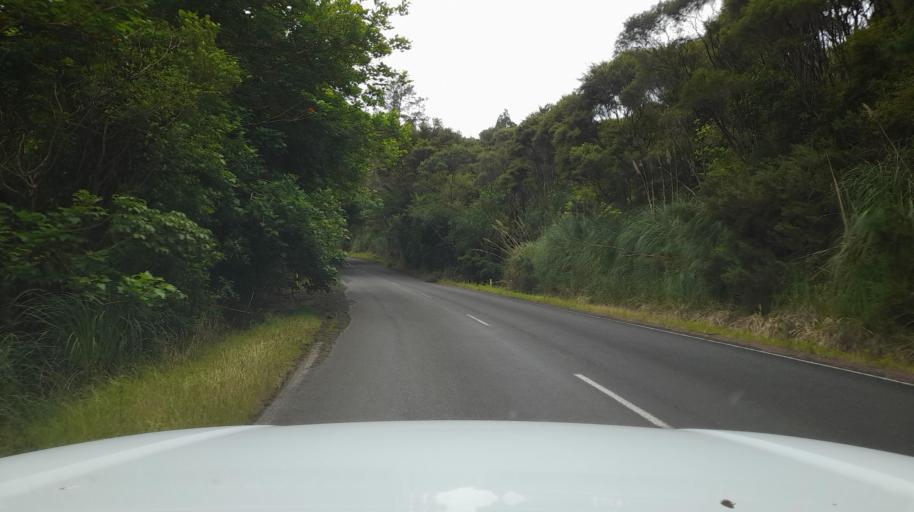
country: NZ
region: Northland
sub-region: Far North District
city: Kaitaia
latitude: -35.3594
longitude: 173.4597
